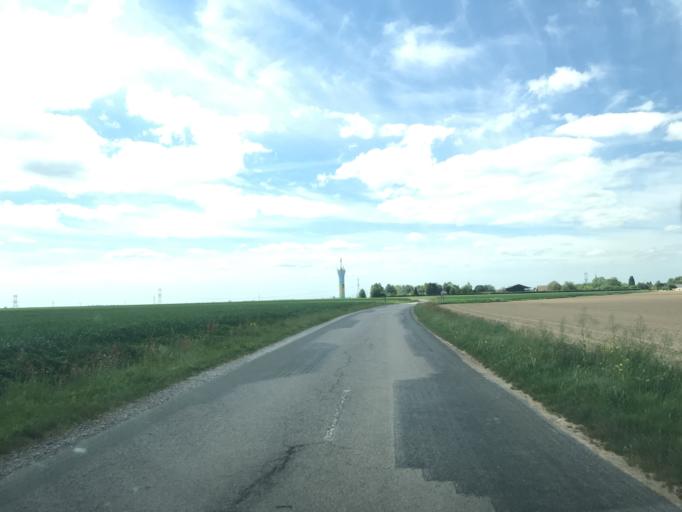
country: FR
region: Haute-Normandie
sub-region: Departement de l'Eure
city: Le Neubourg
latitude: 49.1487
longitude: 0.8715
